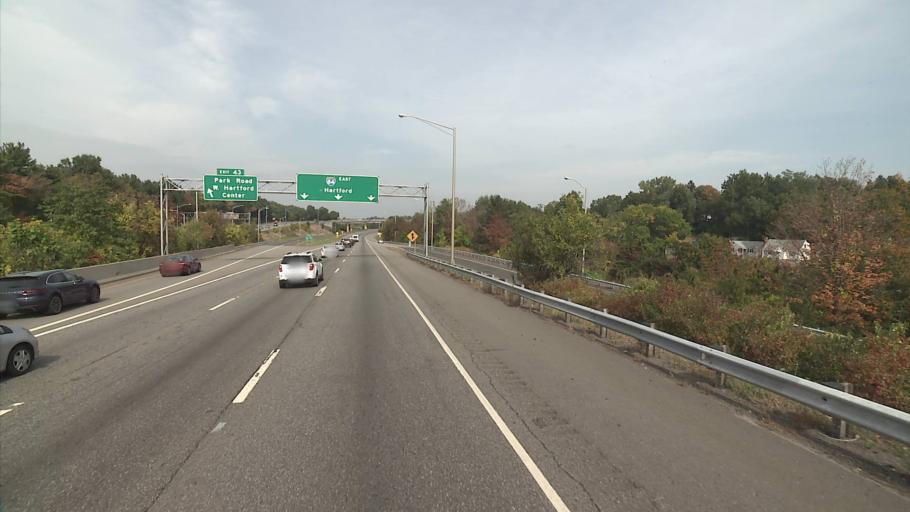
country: US
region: Connecticut
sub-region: Hartford County
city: West Hartford
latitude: 41.7434
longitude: -72.7348
